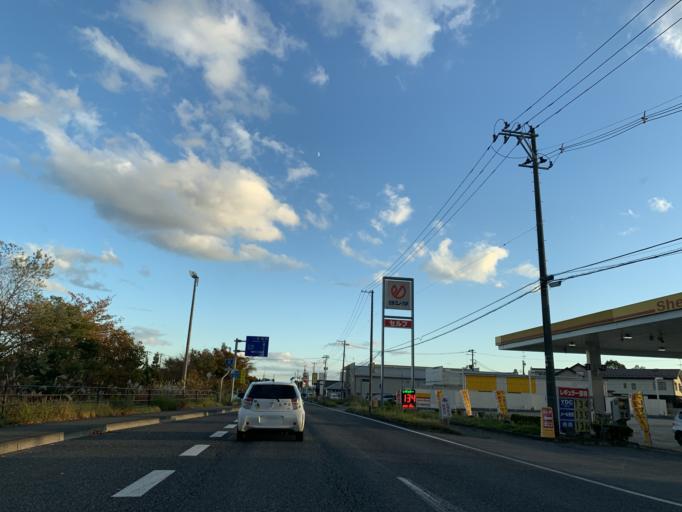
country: JP
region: Iwate
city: Kitakami
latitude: 39.2193
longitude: 141.0997
